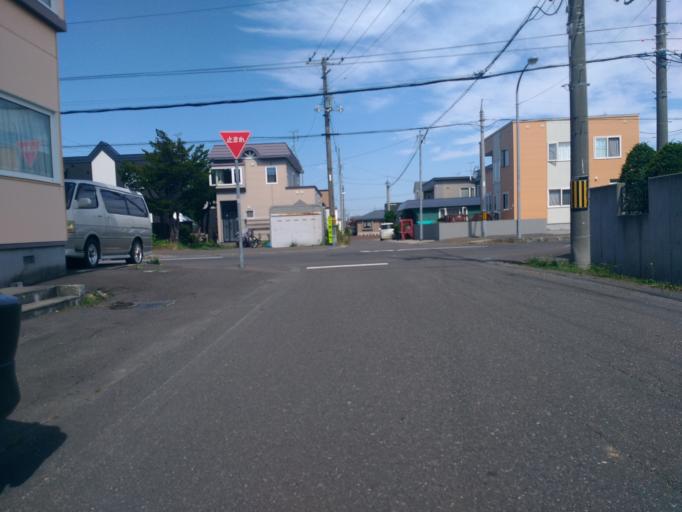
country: JP
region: Hokkaido
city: Ebetsu
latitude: 43.0814
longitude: 141.5076
